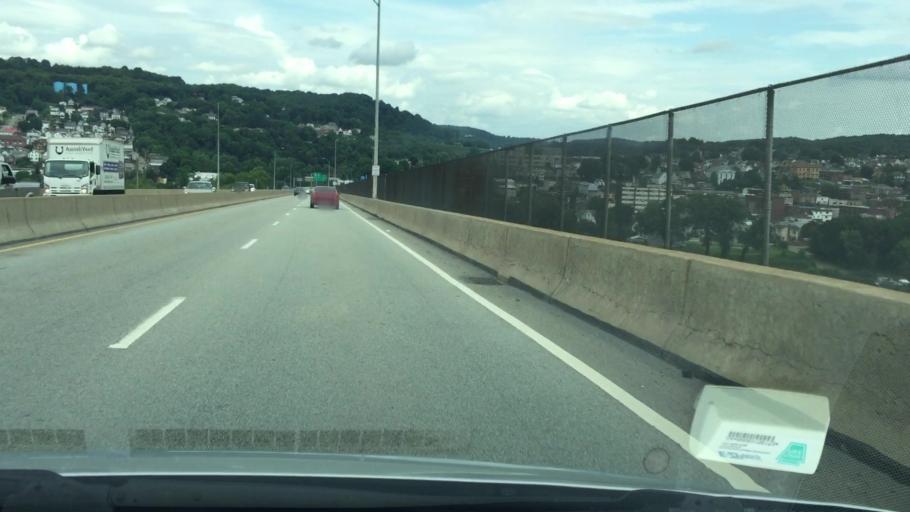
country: US
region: Pennsylvania
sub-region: Allegheny County
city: Tarentum
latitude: 40.5955
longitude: -79.7539
